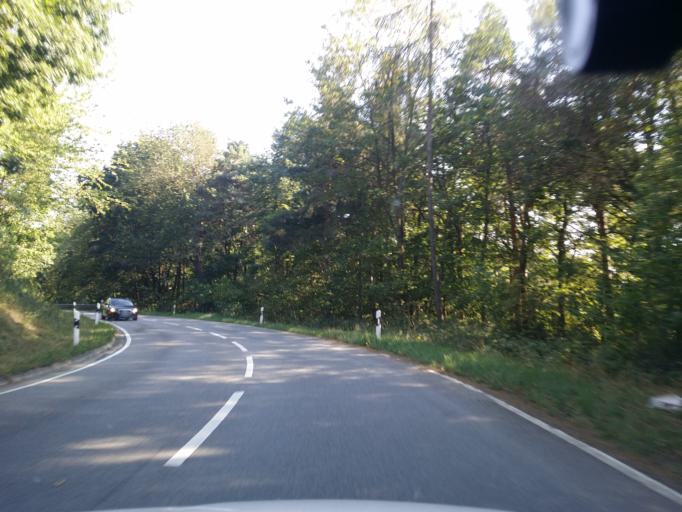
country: DE
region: Hesse
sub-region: Regierungsbezirk Darmstadt
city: Idstein
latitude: 50.2110
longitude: 8.2472
